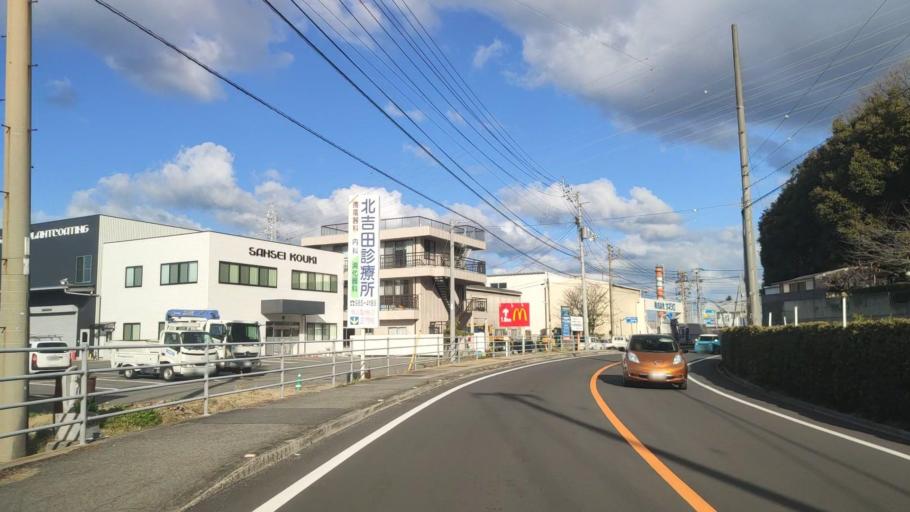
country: JP
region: Ehime
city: Masaki-cho
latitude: 33.8419
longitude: 132.7080
